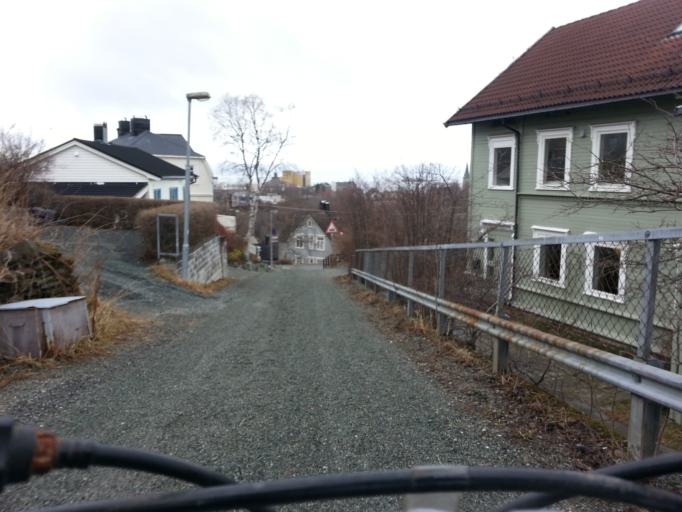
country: NO
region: Sor-Trondelag
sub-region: Trondheim
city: Trondheim
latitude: 63.4239
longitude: 10.3723
